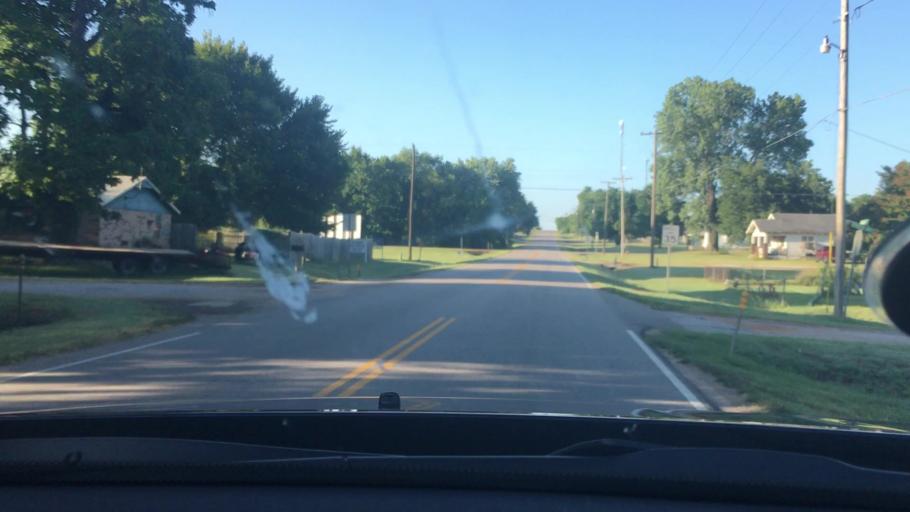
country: US
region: Oklahoma
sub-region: Murray County
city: Sulphur
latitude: 34.6265
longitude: -96.8447
